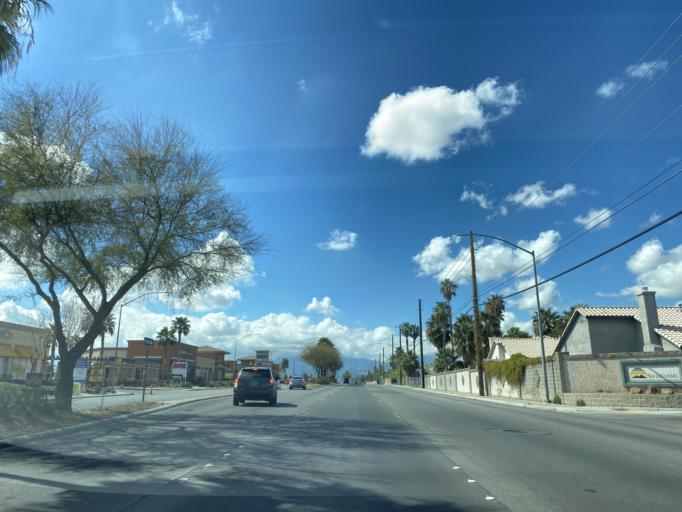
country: US
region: Nevada
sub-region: Clark County
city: North Las Vegas
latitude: 36.2395
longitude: -115.1816
